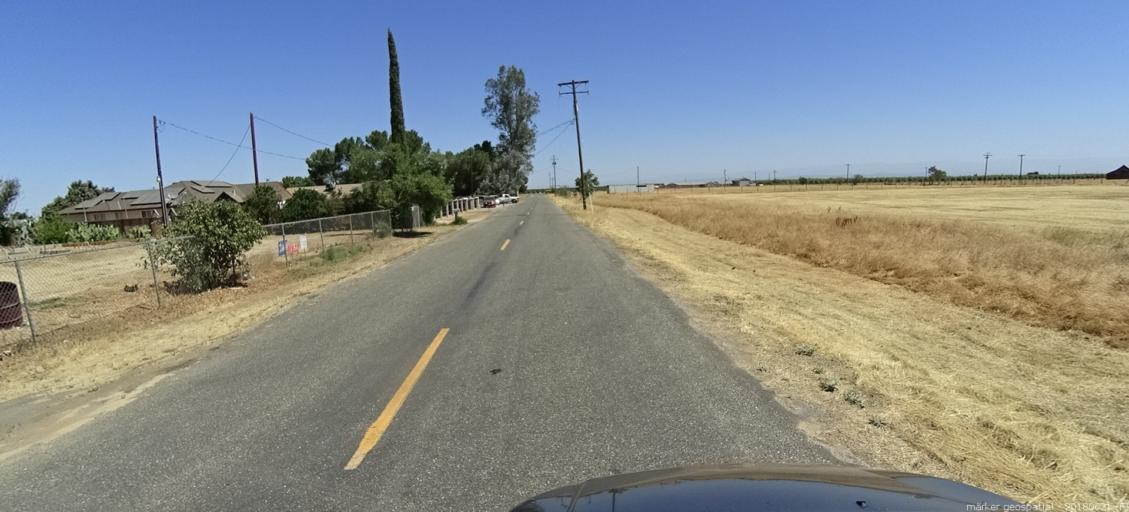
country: US
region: California
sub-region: Madera County
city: Parksdale
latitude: 36.9103
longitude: -119.9576
